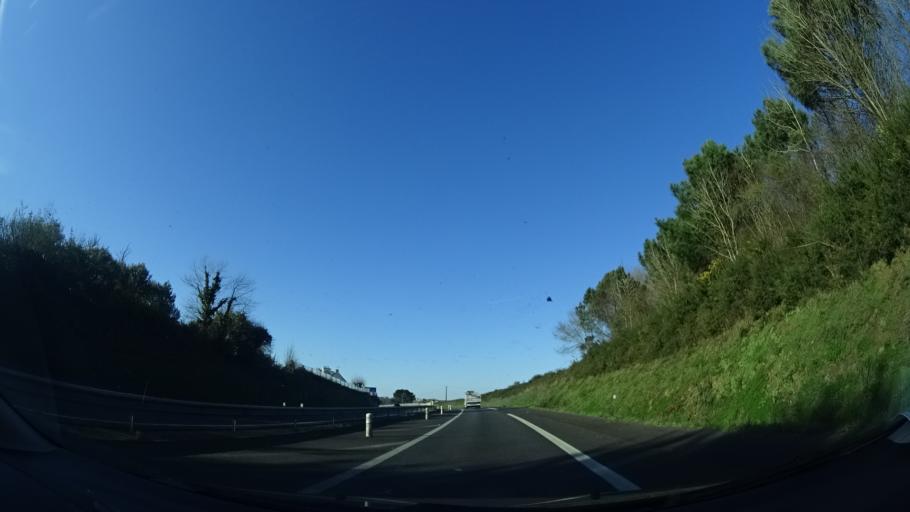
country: FR
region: Brittany
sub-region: Departement du Finistere
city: Henvic
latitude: 48.6449
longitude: -3.9412
